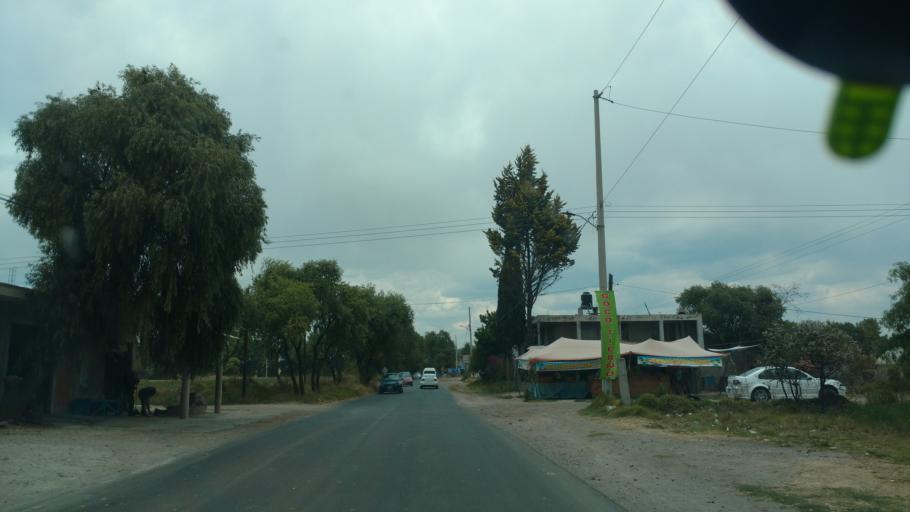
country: MX
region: Puebla
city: San Miguel Xoxtla
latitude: 19.1837
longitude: -98.2966
